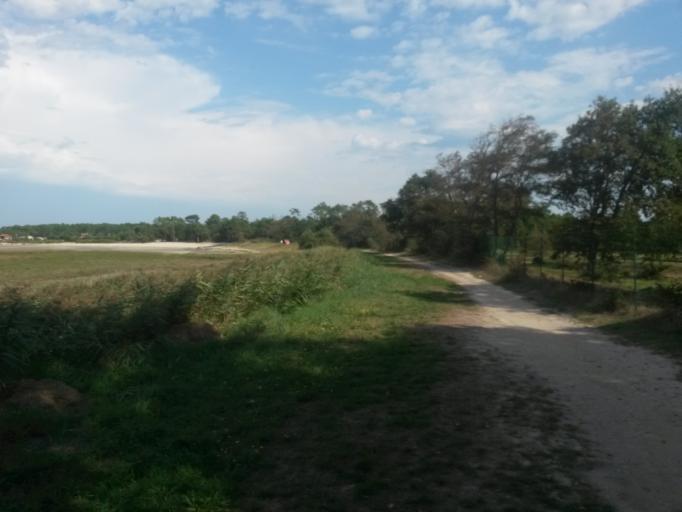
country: FR
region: Aquitaine
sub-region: Departement de la Gironde
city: Lanton
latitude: 44.7050
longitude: -1.0523
